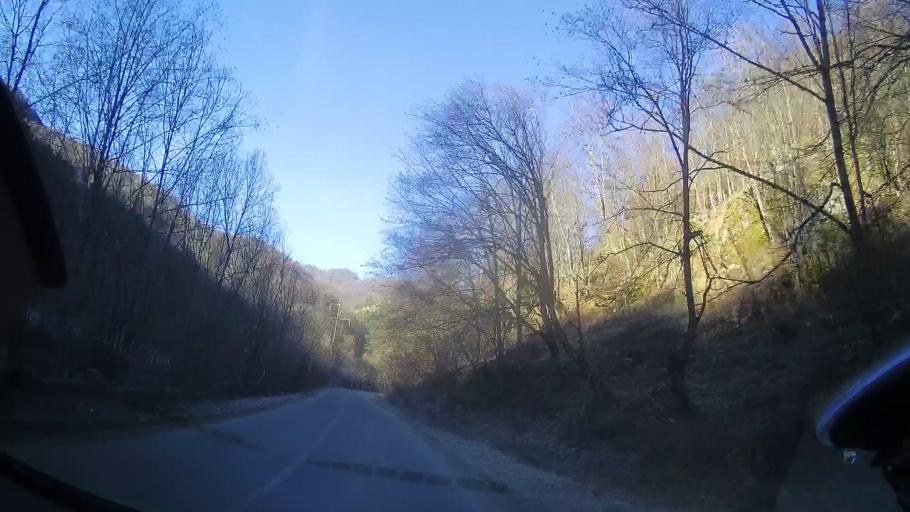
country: RO
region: Cluj
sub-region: Comuna Sacueu
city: Sacuieu
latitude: 46.8330
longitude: 22.8646
